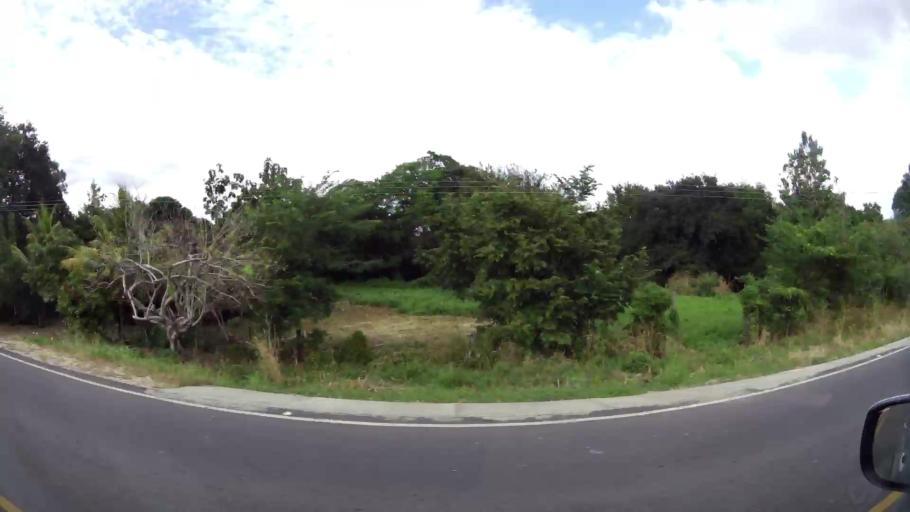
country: CR
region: Guanacaste
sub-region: Canton de Nicoya
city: Nicoya
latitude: 10.1439
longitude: -85.3244
